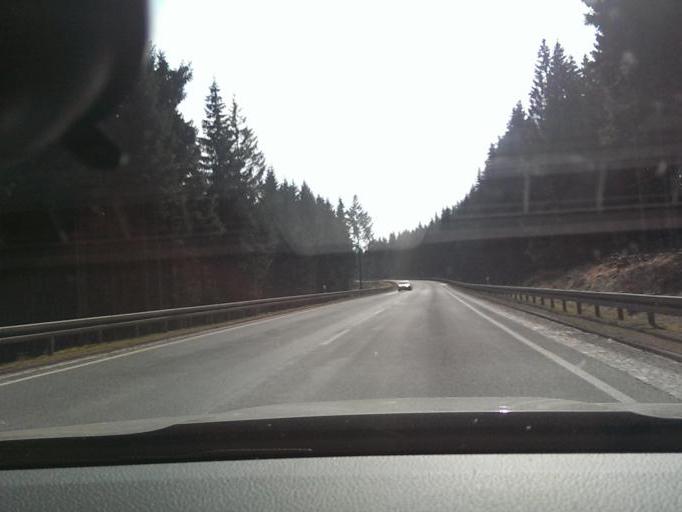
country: DE
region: Thuringia
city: Luisenthal
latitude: 50.7540
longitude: 10.7411
